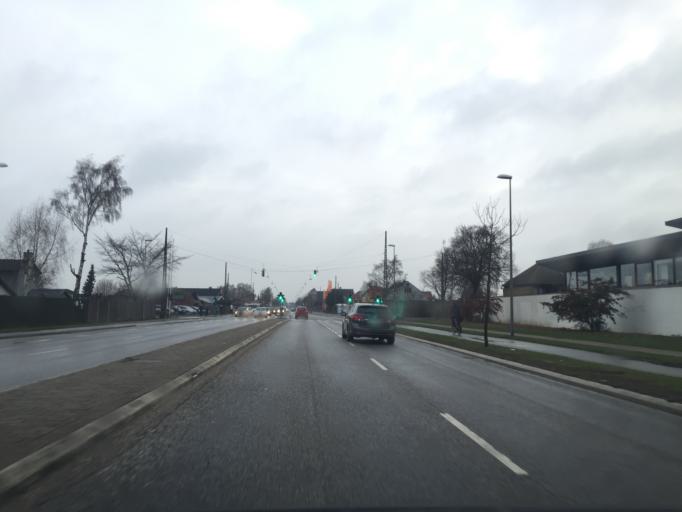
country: DK
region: Capital Region
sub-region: Tarnby Kommune
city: Tarnby
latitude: 55.6372
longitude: 12.6003
